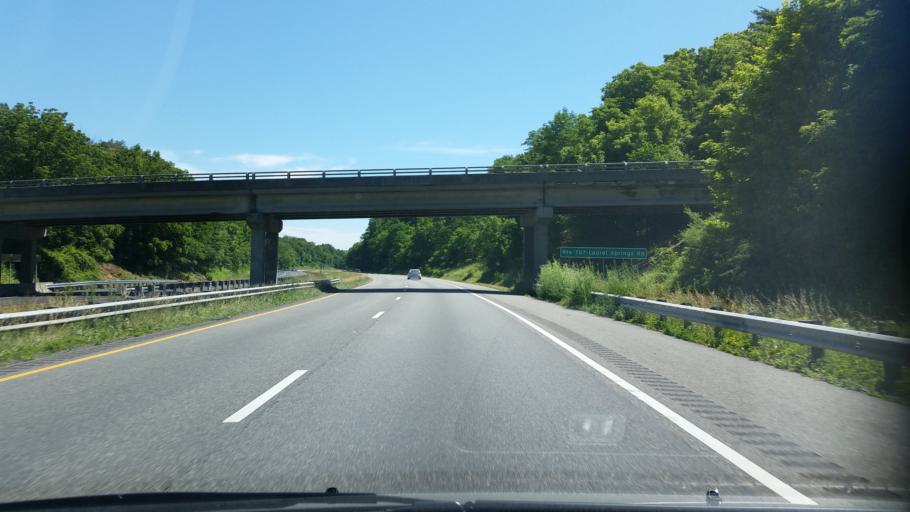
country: US
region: Virginia
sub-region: Smyth County
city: Adwolf
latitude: 36.8137
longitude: -81.5607
